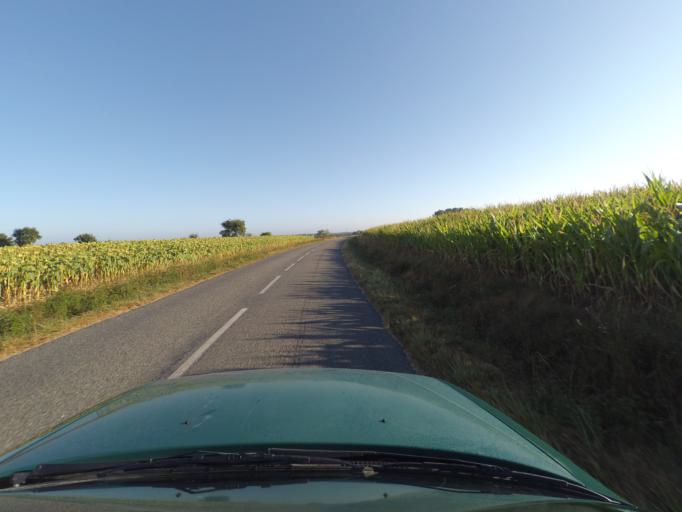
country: FR
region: Pays de la Loire
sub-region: Departement de la Loire-Atlantique
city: Montbert
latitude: 47.0695
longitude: -1.4708
